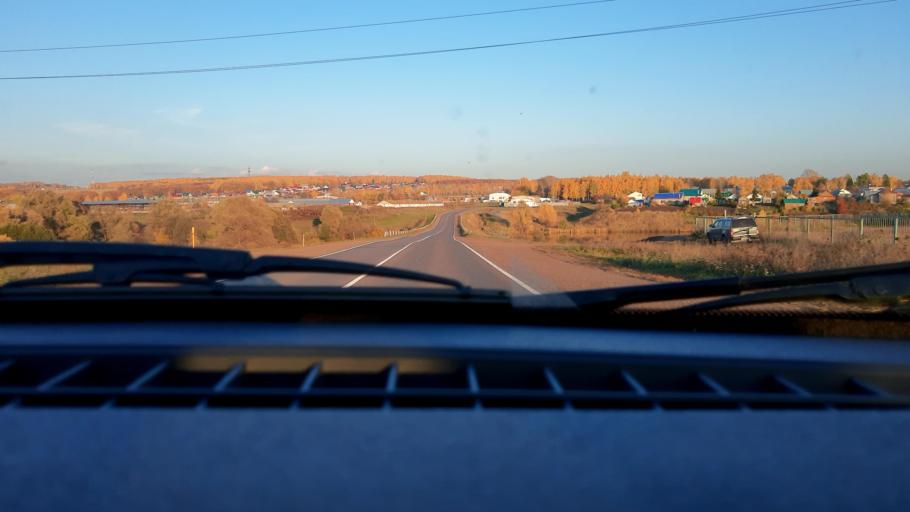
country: RU
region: Bashkortostan
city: Avdon
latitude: 54.8217
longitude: 55.6828
